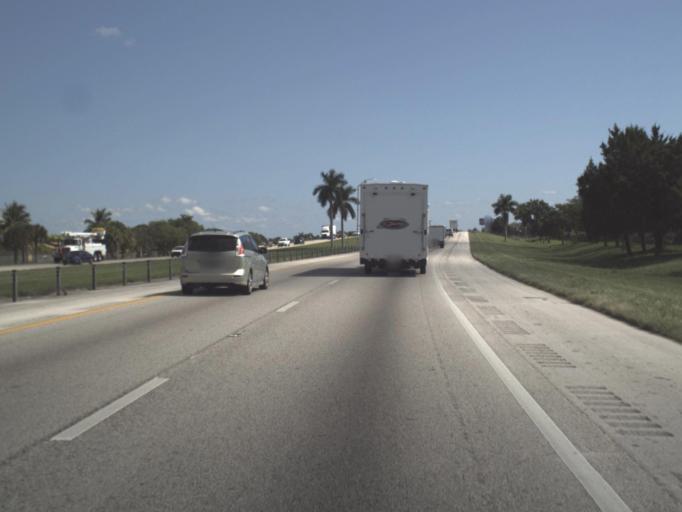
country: US
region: Florida
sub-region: Miami-Dade County
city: Princeton
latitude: 25.5284
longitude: -80.3926
